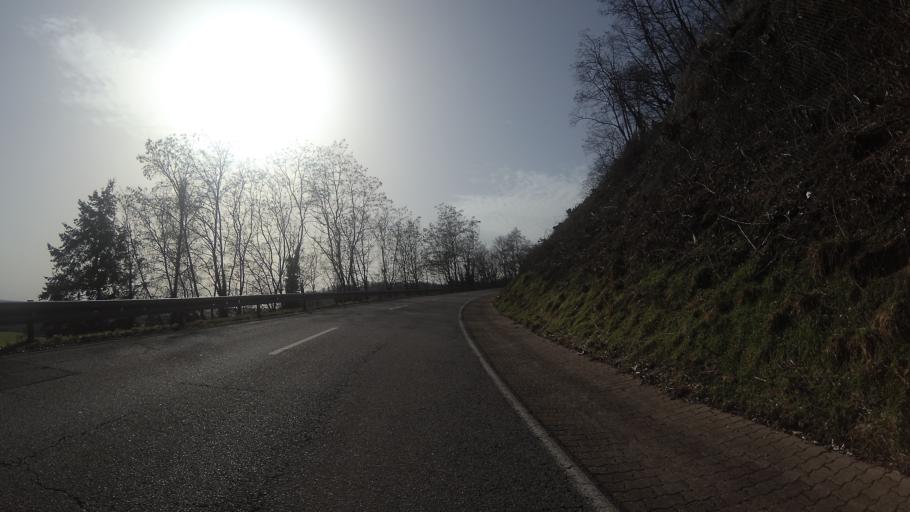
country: DE
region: Saarland
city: Uberherrn
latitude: 49.2694
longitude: 6.7056
